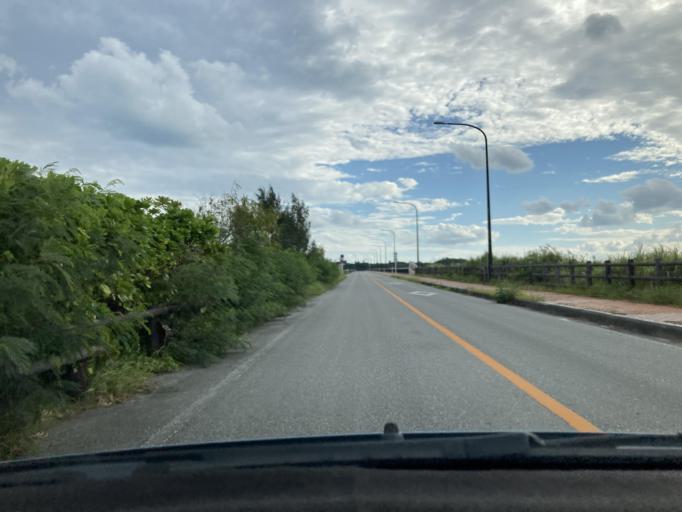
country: JP
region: Okinawa
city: Katsuren-haebaru
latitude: 26.3377
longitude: 127.9552
